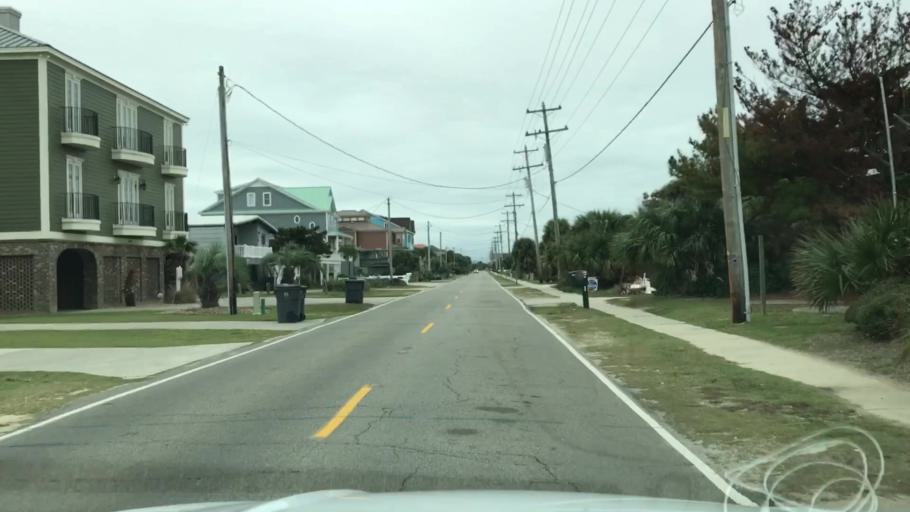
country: US
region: South Carolina
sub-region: Georgetown County
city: Murrells Inlet
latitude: 33.5596
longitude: -79.0134
